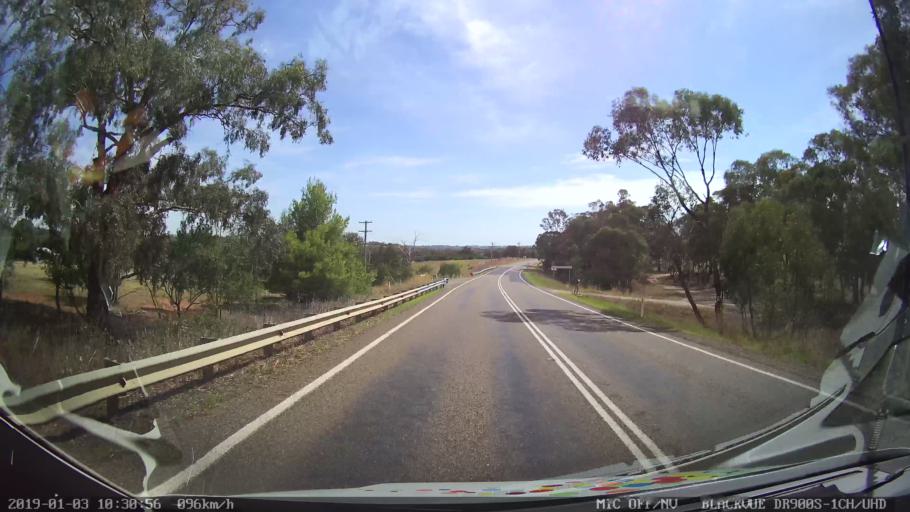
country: AU
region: New South Wales
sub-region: Young
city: Young
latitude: -34.3562
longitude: 148.2726
